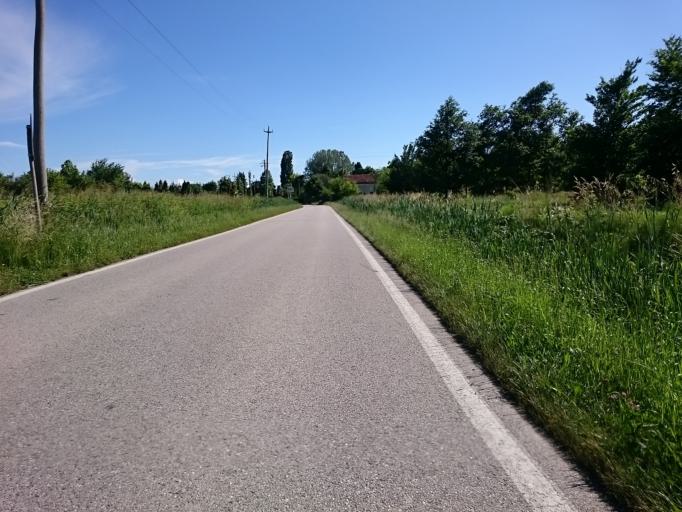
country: IT
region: Veneto
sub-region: Provincia di Padova
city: Saonara
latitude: 45.3579
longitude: 11.9727
